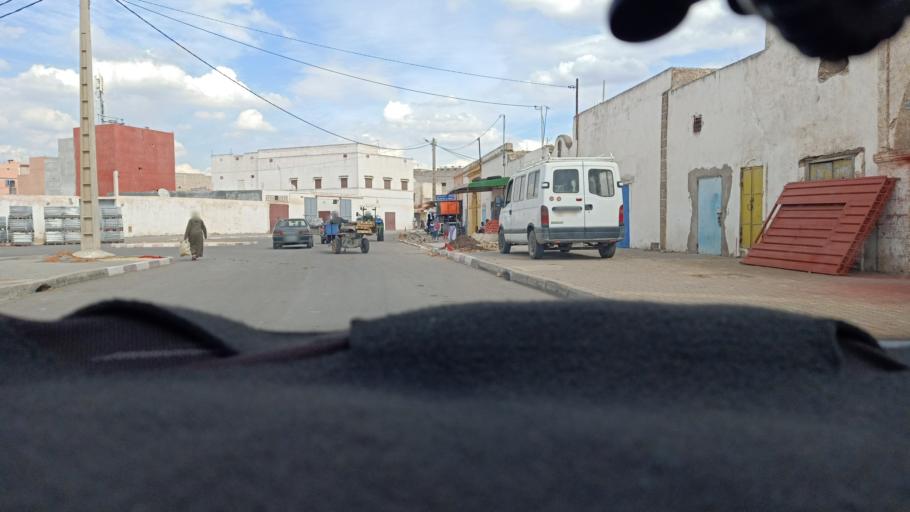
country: MA
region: Doukkala-Abda
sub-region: Safi
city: Youssoufia
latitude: 32.3466
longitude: -8.8420
